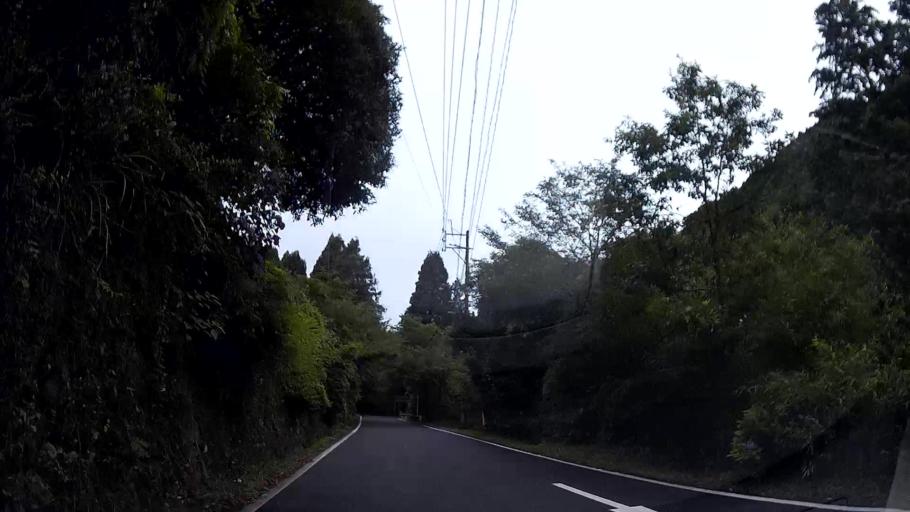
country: JP
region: Kumamoto
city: Kikuchi
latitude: 33.1012
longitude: 130.9606
